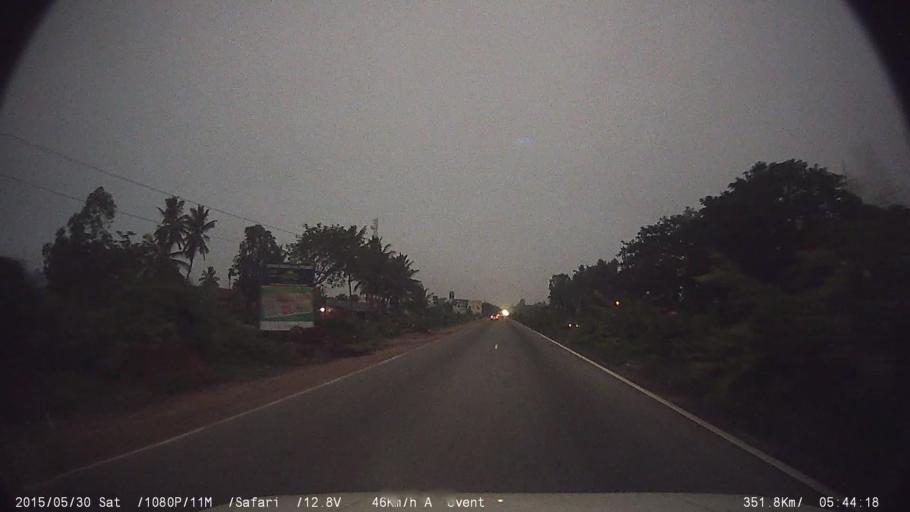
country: IN
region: Karnataka
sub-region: Mandya
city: Mandya
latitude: 12.5065
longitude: 76.8341
